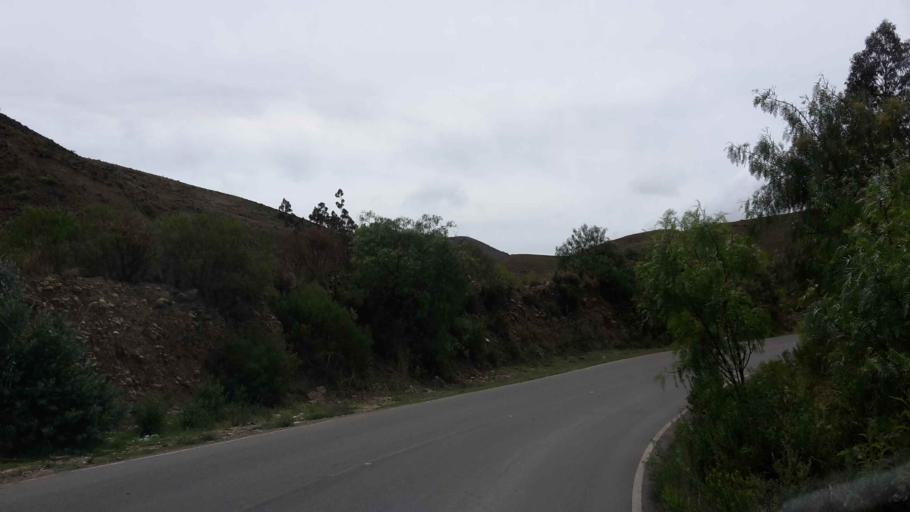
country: BO
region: Cochabamba
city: Colomi
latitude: -17.4009
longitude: -65.7993
